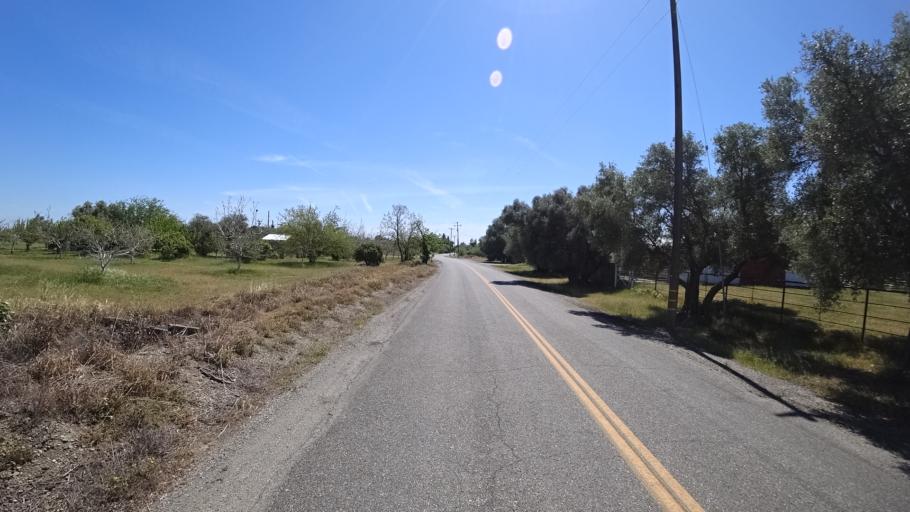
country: US
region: California
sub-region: Glenn County
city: Orland
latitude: 39.7405
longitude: -122.1595
